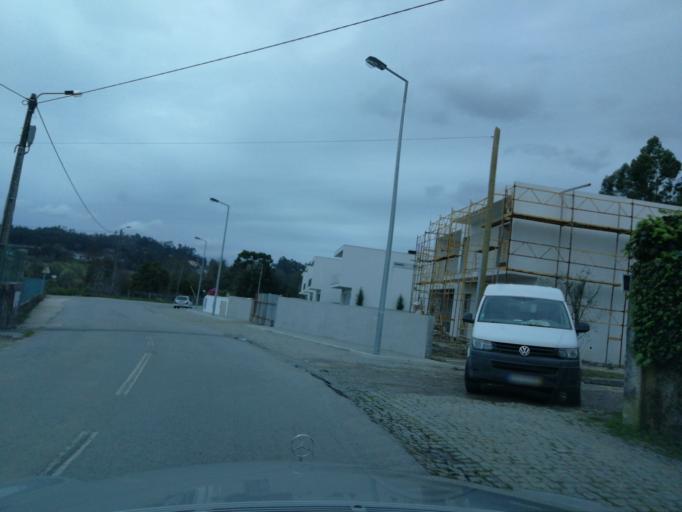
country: PT
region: Braga
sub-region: Braga
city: Oliveira
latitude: 41.4812
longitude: -8.4711
